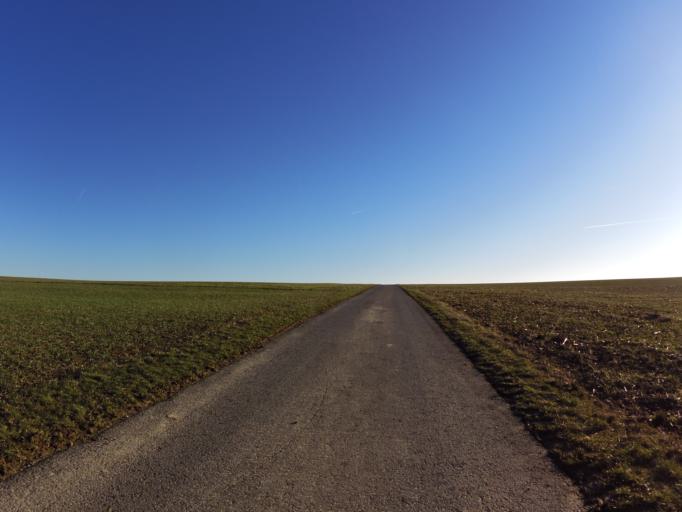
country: DE
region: Bavaria
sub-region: Regierungsbezirk Unterfranken
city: Estenfeld
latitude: 49.8493
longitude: 9.9980
